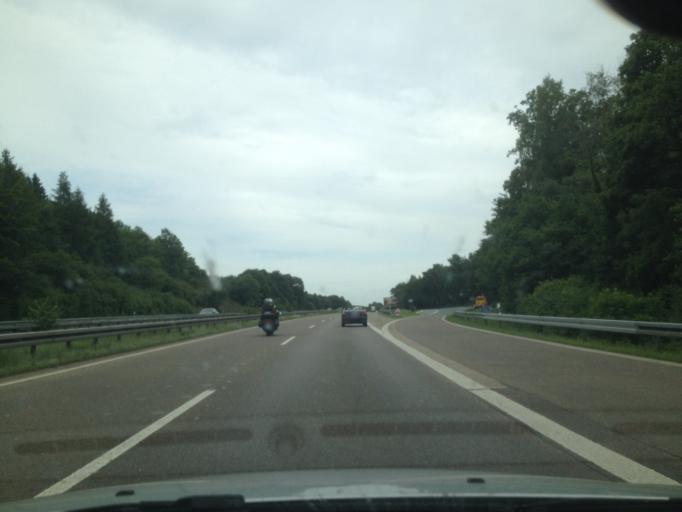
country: DE
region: North Rhine-Westphalia
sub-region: Regierungsbezirk Arnsberg
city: Drolshagen
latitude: 51.0467
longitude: 7.7952
